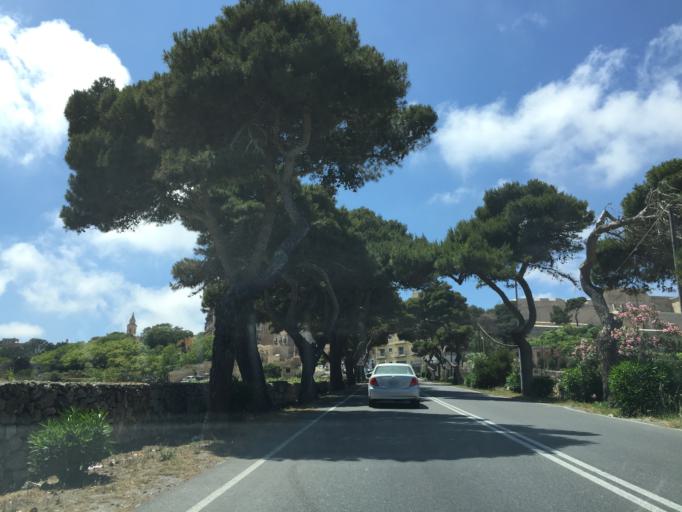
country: MT
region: L-Imdina
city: Imdina
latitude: 35.8832
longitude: 14.4067
